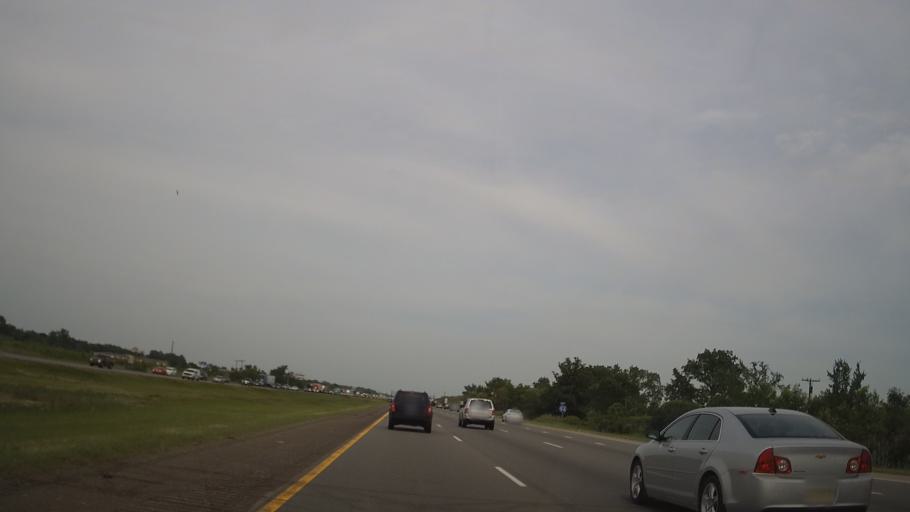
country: US
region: Michigan
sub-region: Wayne County
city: Romulus
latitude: 42.2342
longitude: -83.3603
